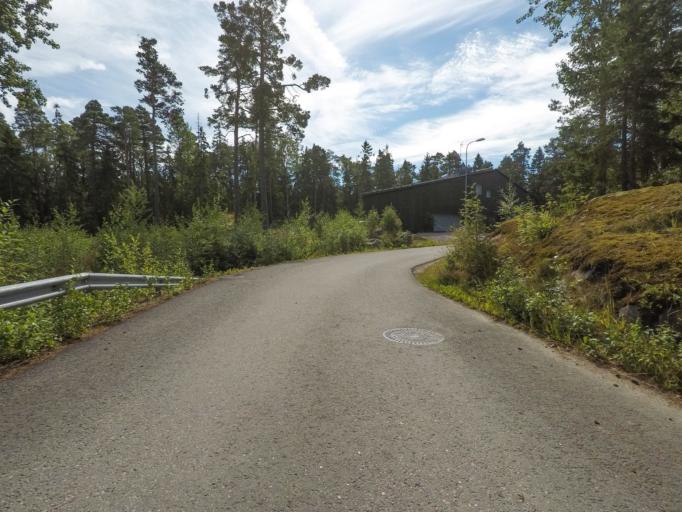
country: FI
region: Uusimaa
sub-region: Helsinki
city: Vantaa
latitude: 60.1668
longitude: 25.0909
